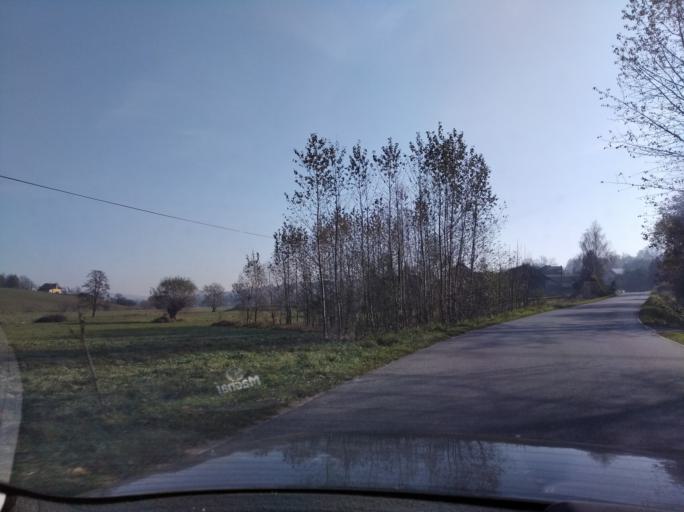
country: PL
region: Subcarpathian Voivodeship
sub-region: Powiat ropczycko-sedziszowski
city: Wielopole Skrzynskie
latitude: 49.9475
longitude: 21.6002
